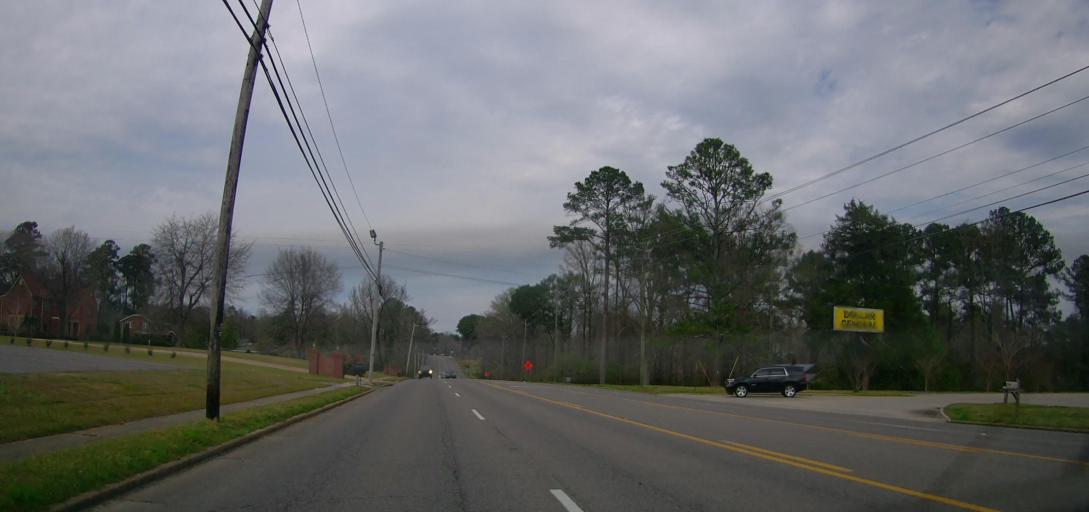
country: US
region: Alabama
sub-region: Marion County
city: Hamilton
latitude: 34.1276
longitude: -87.9899
